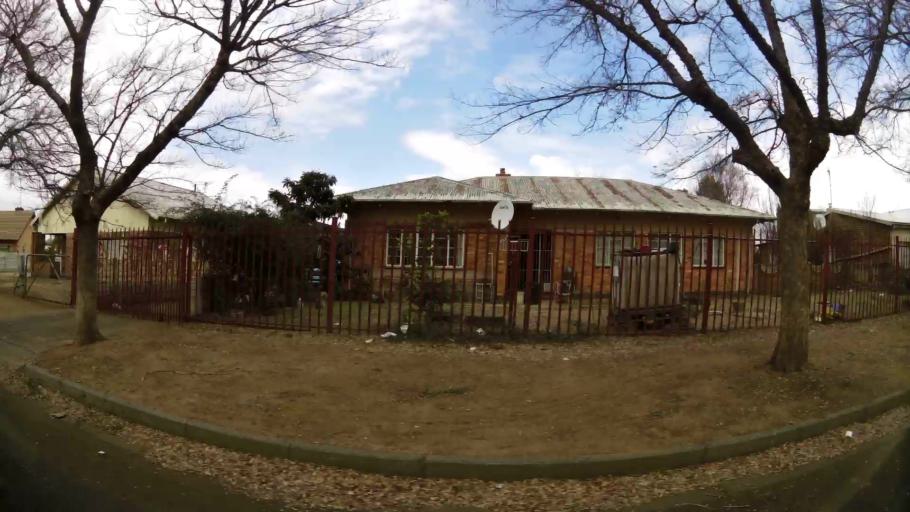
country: ZA
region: Orange Free State
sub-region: Fezile Dabi District Municipality
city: Kroonstad
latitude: -27.6328
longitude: 27.2303
